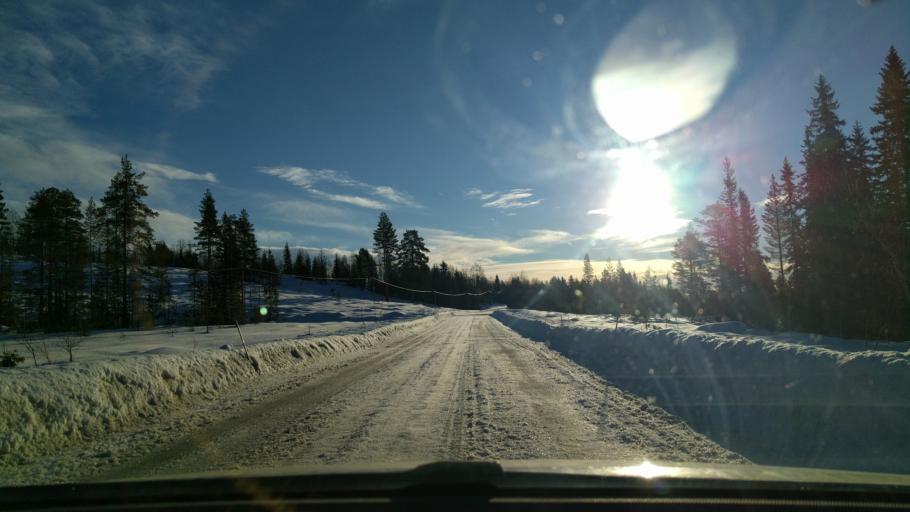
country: NO
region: Hedmark
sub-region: Trysil
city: Innbygda
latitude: 61.0834
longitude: 12.2099
